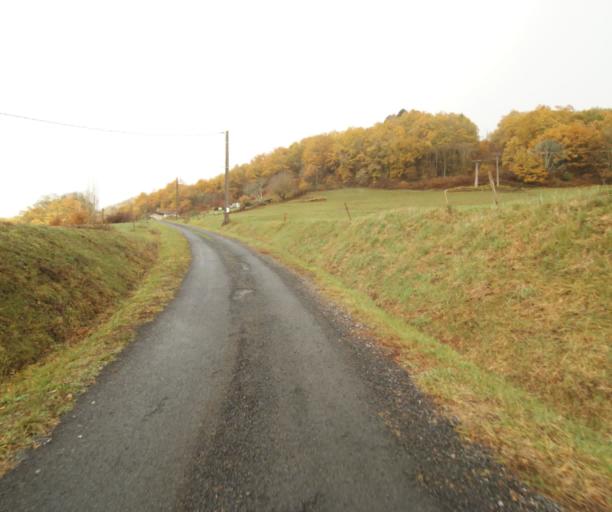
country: FR
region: Limousin
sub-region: Departement de la Correze
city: Cornil
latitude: 45.1814
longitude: 1.6505
